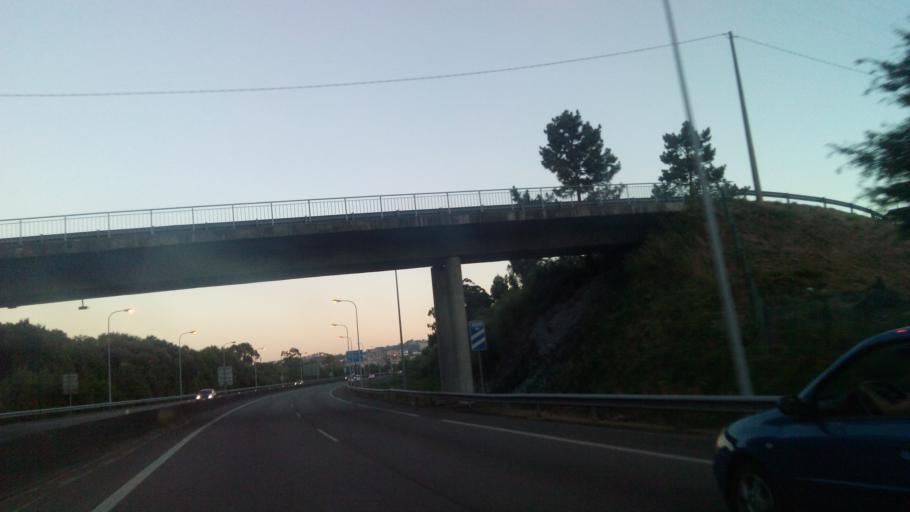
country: ES
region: Galicia
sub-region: Provincia de Pontevedra
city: Pontevedra
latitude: 42.4447
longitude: -8.6483
